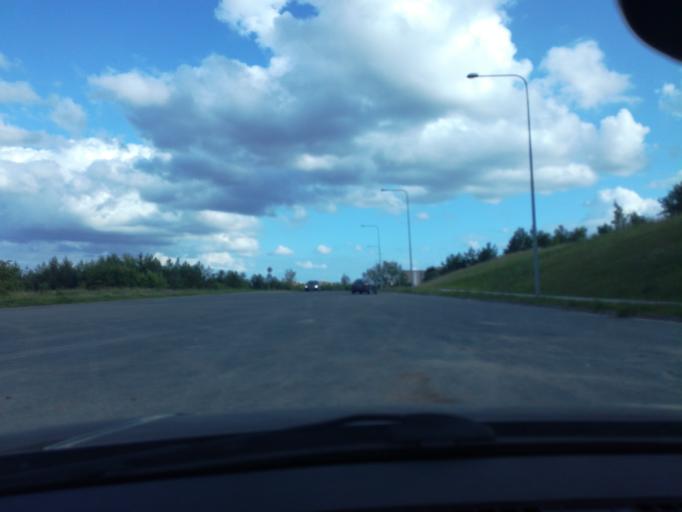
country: LT
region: Alytaus apskritis
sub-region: Alytus
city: Alytus
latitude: 54.4035
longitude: 24.0137
